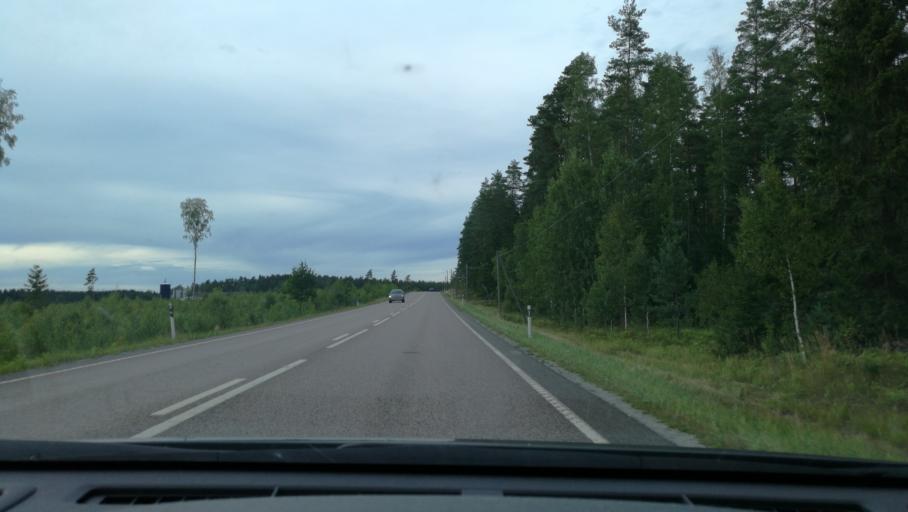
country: SE
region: Soedermanland
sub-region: Katrineholms Kommun
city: Katrineholm
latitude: 59.1961
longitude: 16.1044
